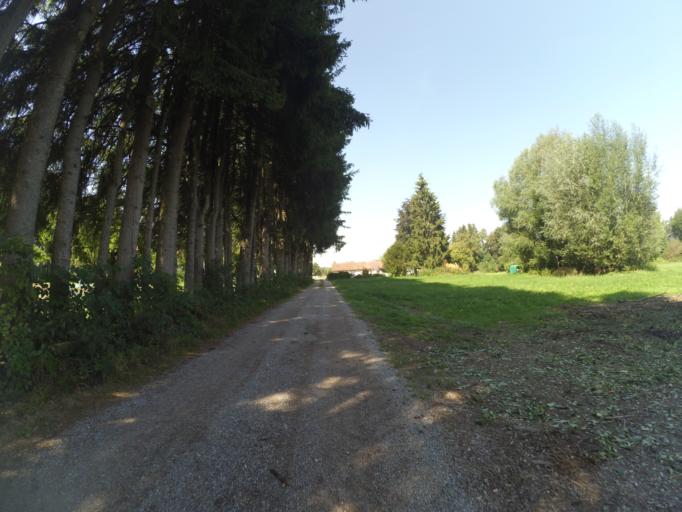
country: DE
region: Bavaria
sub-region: Swabia
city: Lamerdingen
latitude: 48.1084
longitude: 10.7739
